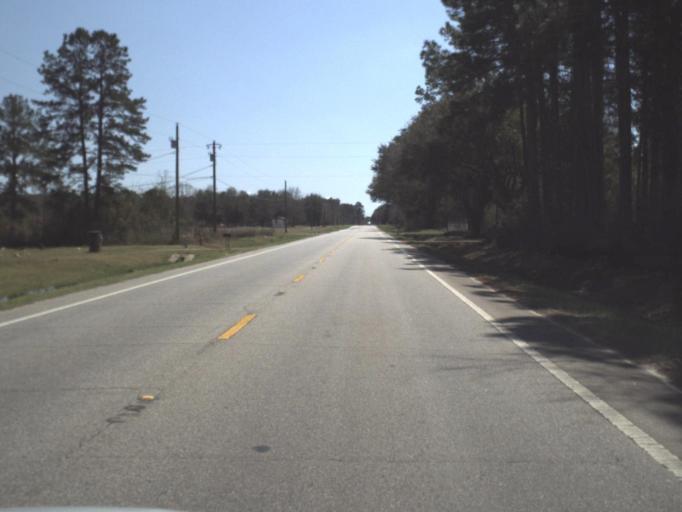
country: US
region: Florida
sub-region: Gadsden County
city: Gretna
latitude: 30.6947
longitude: -84.6235
